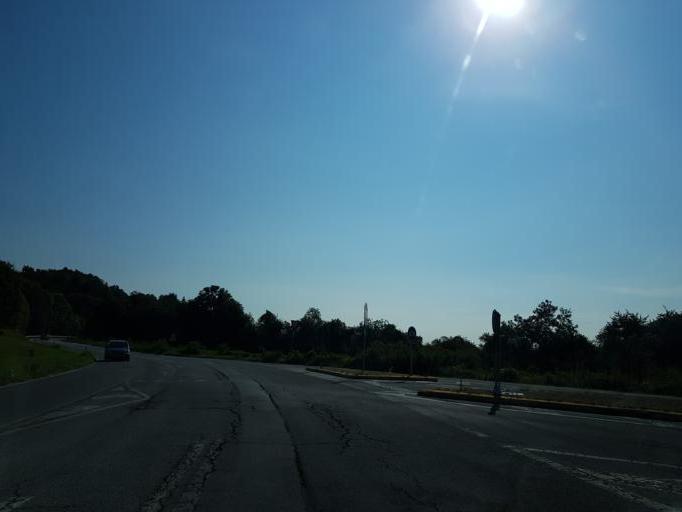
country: IT
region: Piedmont
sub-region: Provincia di Cuneo
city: Tettorosso
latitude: 44.4681
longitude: 7.3204
